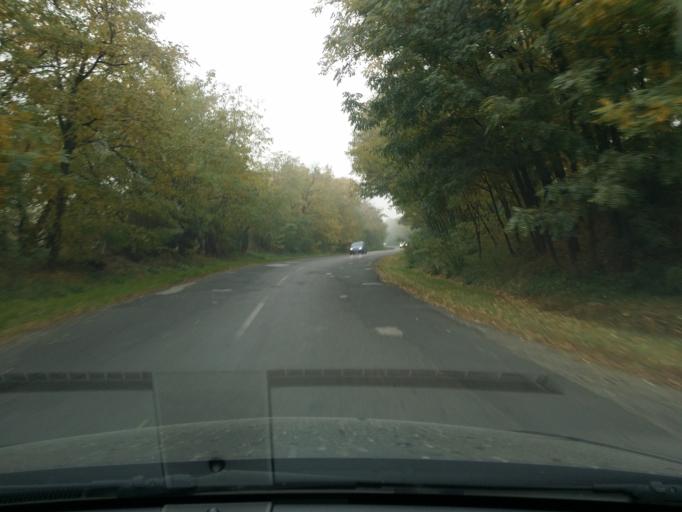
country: HU
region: Szabolcs-Szatmar-Bereg
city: Nyirbogdany
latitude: 48.0681
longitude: 21.8604
